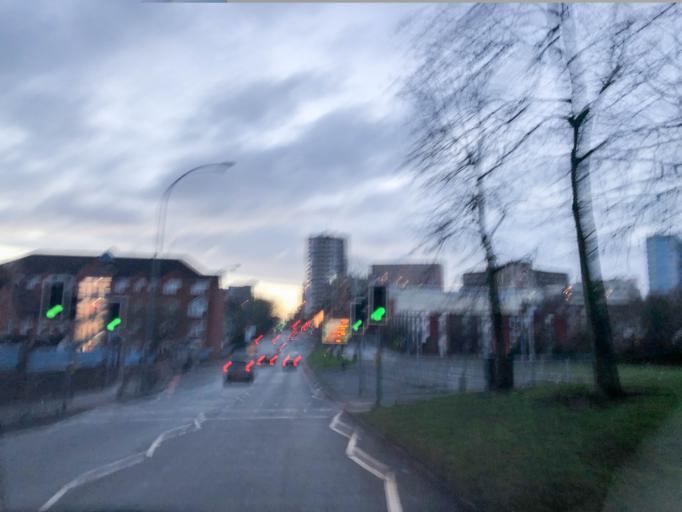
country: GB
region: England
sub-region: City and Borough of Birmingham
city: Birmingham
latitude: 52.4761
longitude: -1.9240
